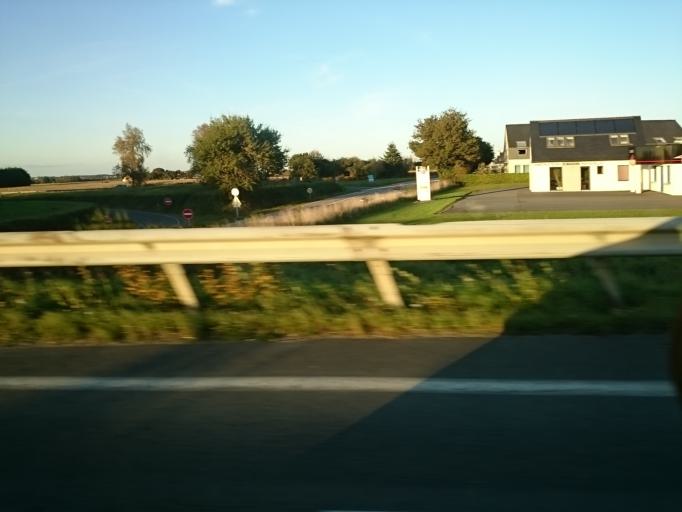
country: FR
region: Brittany
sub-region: Departement du Finistere
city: Morlaix
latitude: 48.5931
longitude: -3.8198
